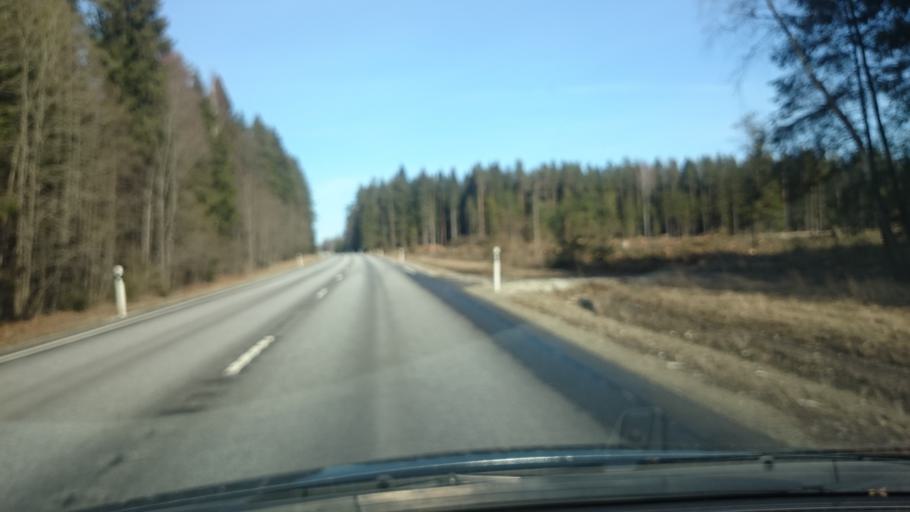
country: EE
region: Jaervamaa
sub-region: Tueri vald
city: Sarevere
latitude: 58.7003
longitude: 25.2598
